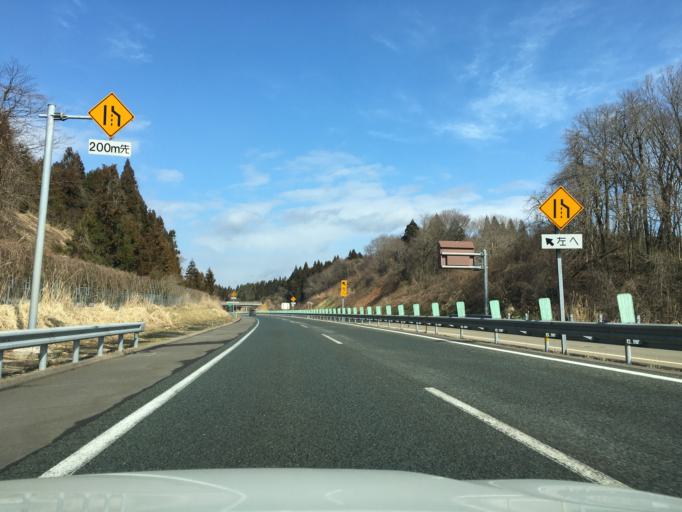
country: JP
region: Akita
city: Akita
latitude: 39.7256
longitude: 140.1808
